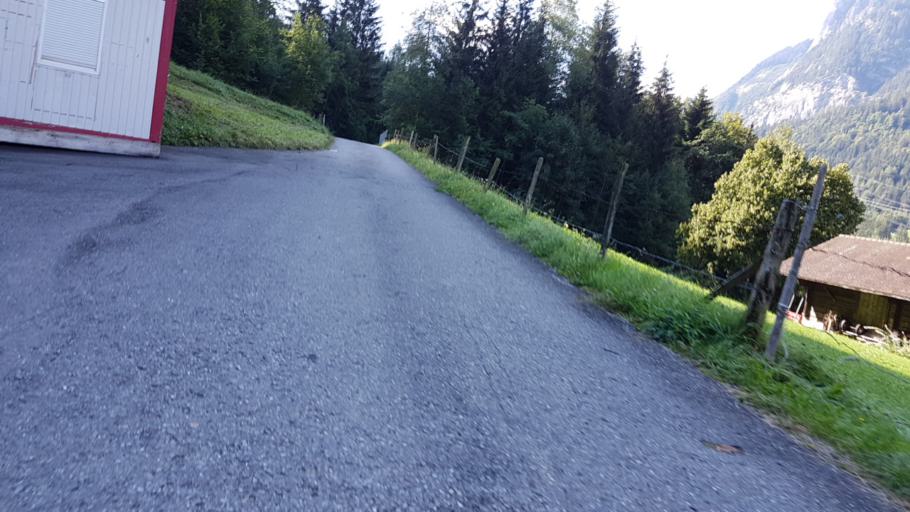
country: CH
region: Bern
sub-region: Frutigen-Niedersimmental District
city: Kandersteg
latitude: 46.5268
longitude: 7.6775
